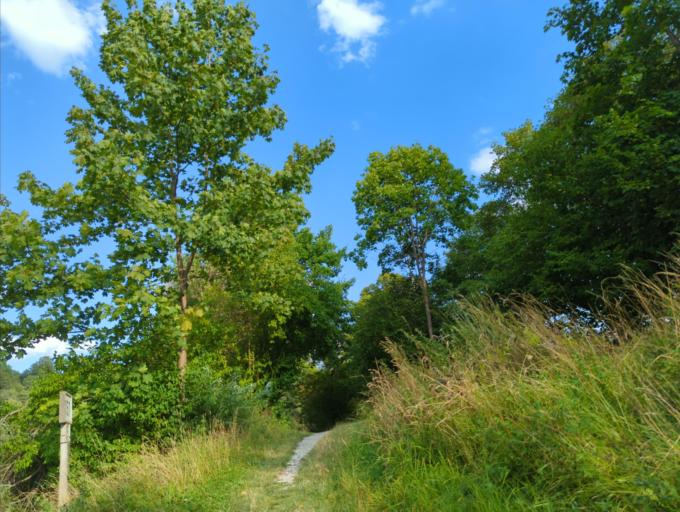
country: DE
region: Bavaria
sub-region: Upper Bavaria
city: Wasserburg am Inn
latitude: 48.0649
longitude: 12.2351
